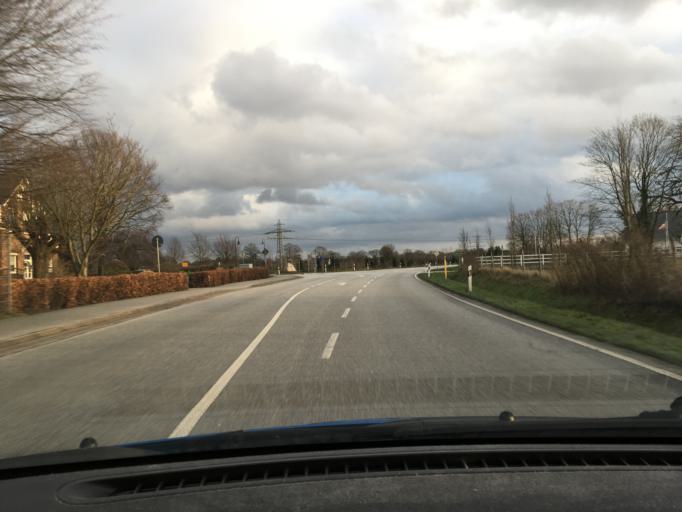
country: DE
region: Schleswig-Holstein
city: Seeth-Ekholt
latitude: 53.7419
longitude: 9.7204
